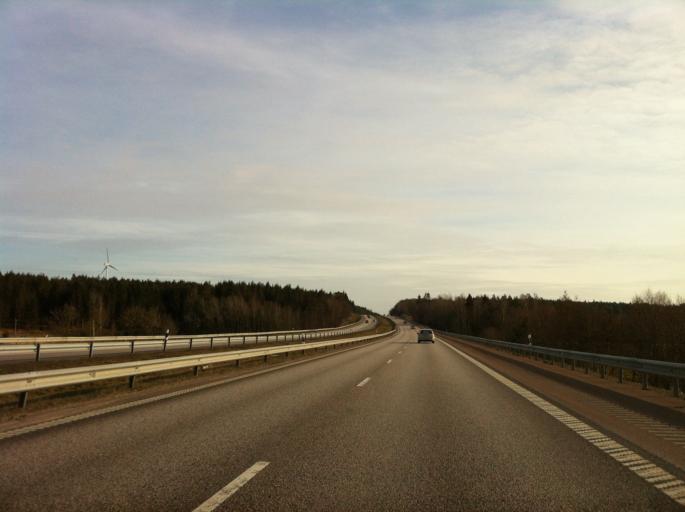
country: SE
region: Halland
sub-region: Kungsbacka Kommun
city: Fjaeras kyrkby
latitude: 57.4137
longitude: 12.1707
